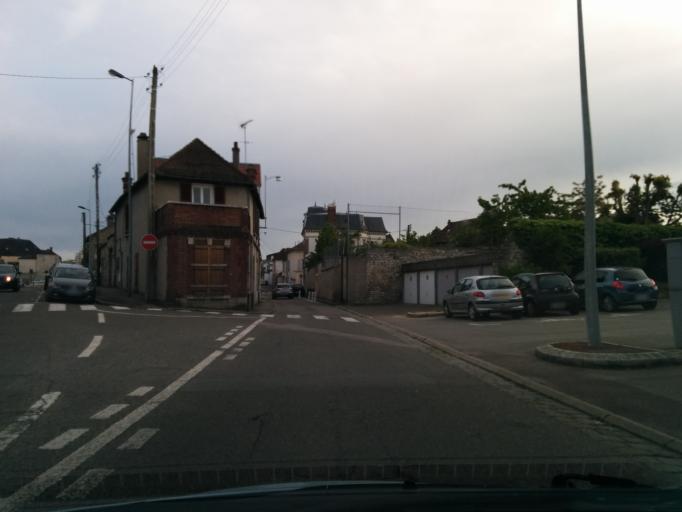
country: FR
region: Ile-de-France
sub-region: Departement des Yvelines
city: Mantes-la-Jolie
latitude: 48.9922
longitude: 1.7147
